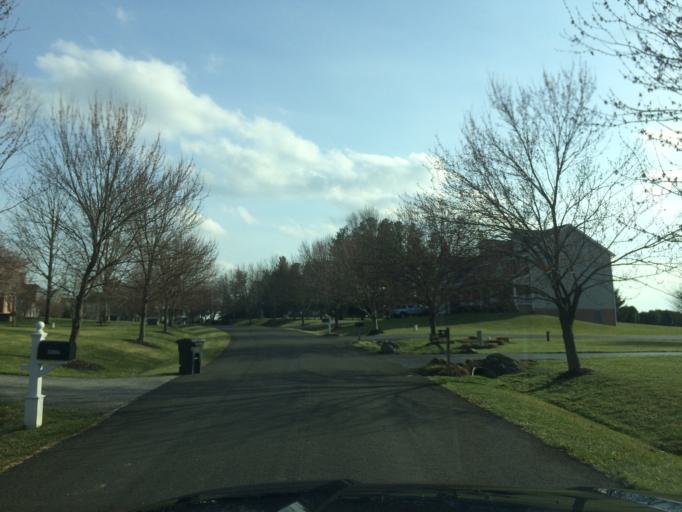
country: US
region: Maryland
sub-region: Carroll County
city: Sykesville
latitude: 39.2818
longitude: -76.9840
